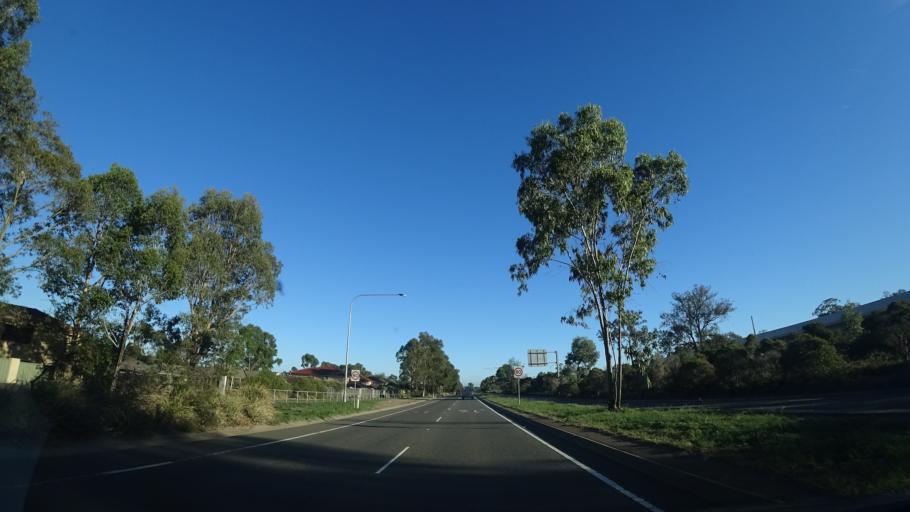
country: AU
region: New South Wales
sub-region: Blacktown
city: Stanhope Gardens
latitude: -33.7187
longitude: 150.9371
